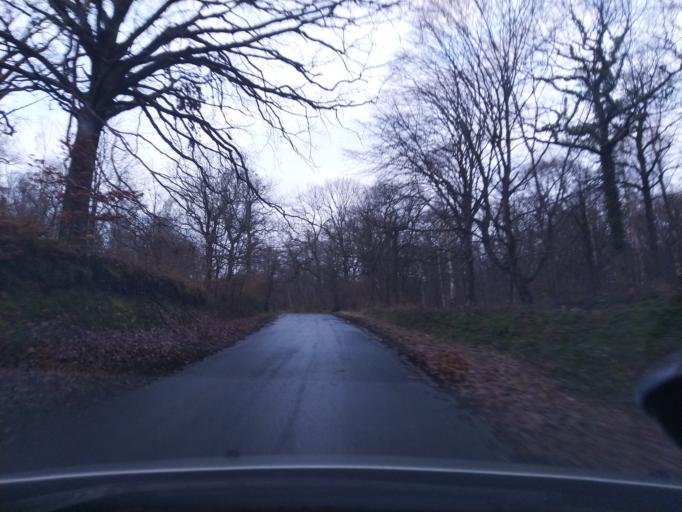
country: FR
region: Haute-Normandie
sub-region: Departement de la Seine-Maritime
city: Saint-Pierre-de-Varengeville
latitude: 49.4920
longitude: 0.9054
